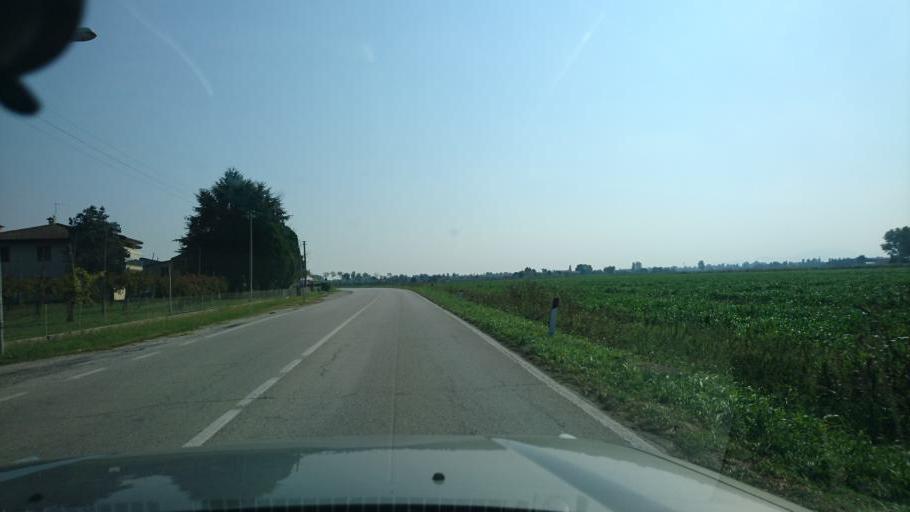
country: IT
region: Veneto
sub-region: Provincia di Vicenza
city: Camisano Vicentino
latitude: 45.5169
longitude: 11.7301
